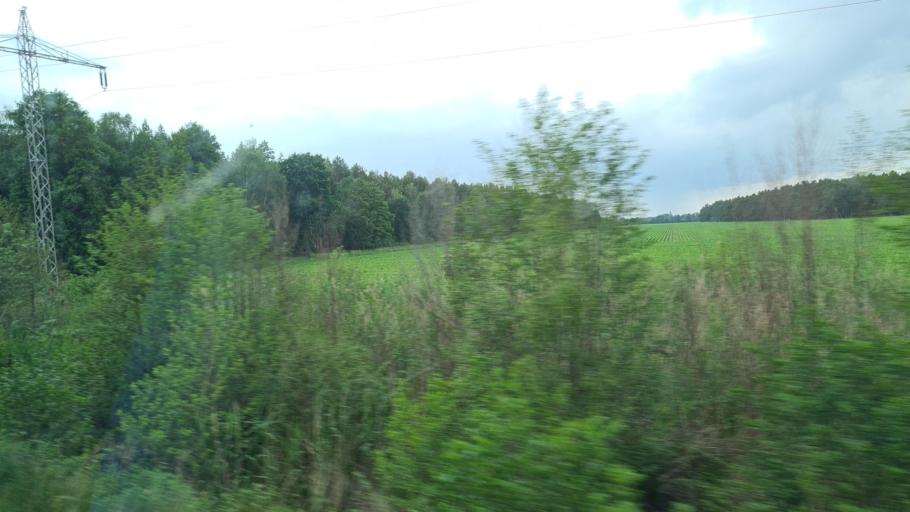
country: DE
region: Brandenburg
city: Schilda
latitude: 51.5895
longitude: 13.3505
